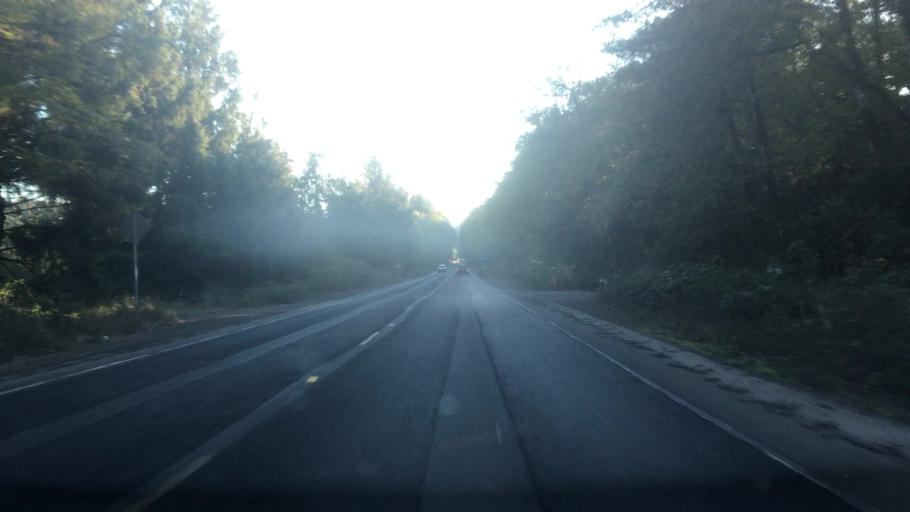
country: US
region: Oregon
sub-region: Clatsop County
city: Cannon Beach
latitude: 45.8964
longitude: -123.9550
